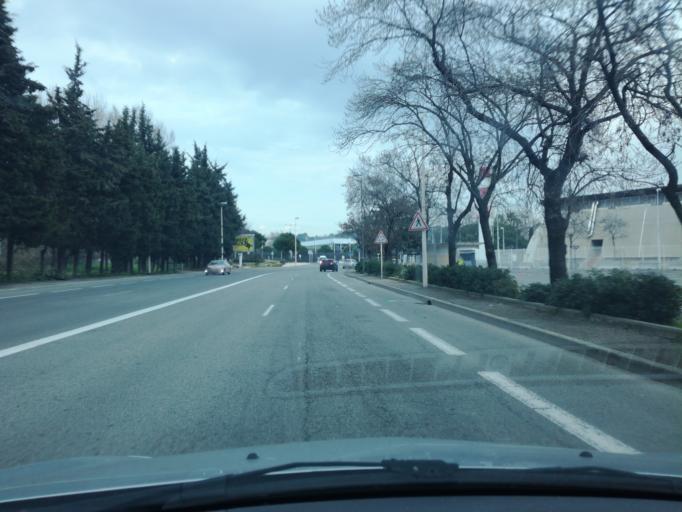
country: FR
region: Provence-Alpes-Cote d'Azur
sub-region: Departement des Alpes-Maritimes
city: Mandelieu-la-Napoule
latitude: 43.5530
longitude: 6.9632
